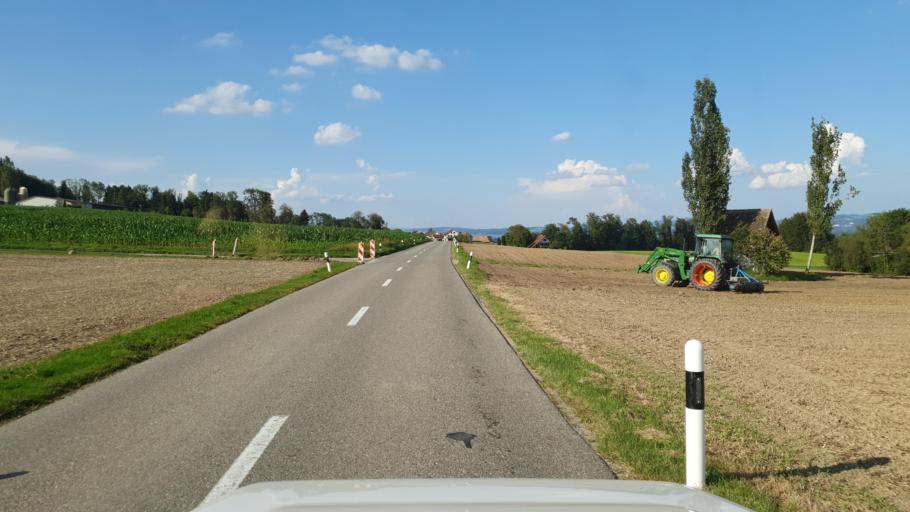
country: CH
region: Aargau
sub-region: Bezirk Muri
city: Auw
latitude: 47.1914
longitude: 8.3580
